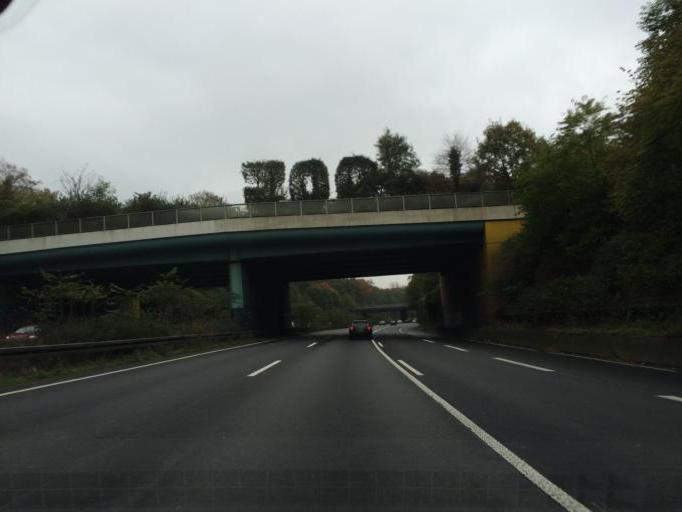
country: DE
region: North Rhine-Westphalia
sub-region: Regierungsbezirk Dusseldorf
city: Duisburg
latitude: 51.4358
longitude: 6.8082
